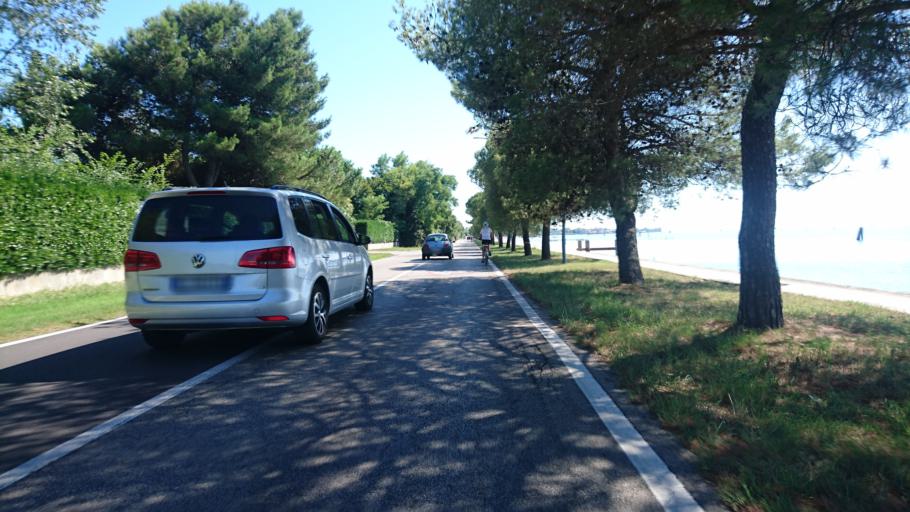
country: IT
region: Veneto
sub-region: Provincia di Venezia
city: San Pietro in Volta
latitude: 45.3649
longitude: 12.3344
